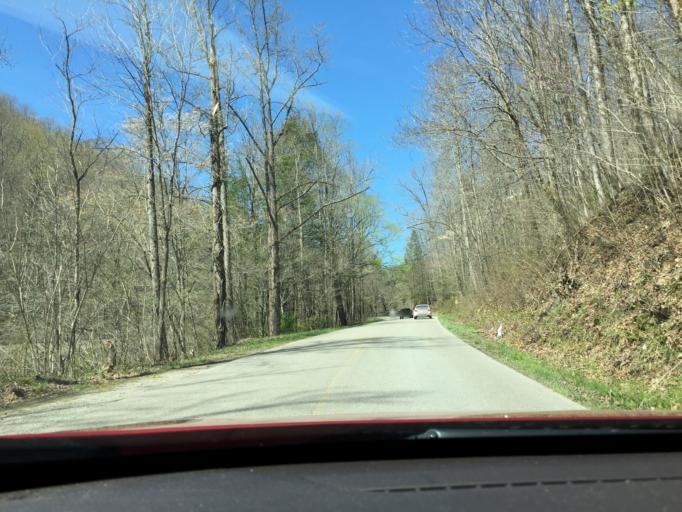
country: US
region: Tennessee
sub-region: Campbell County
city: Caryville
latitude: 36.3551
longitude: -84.2631
